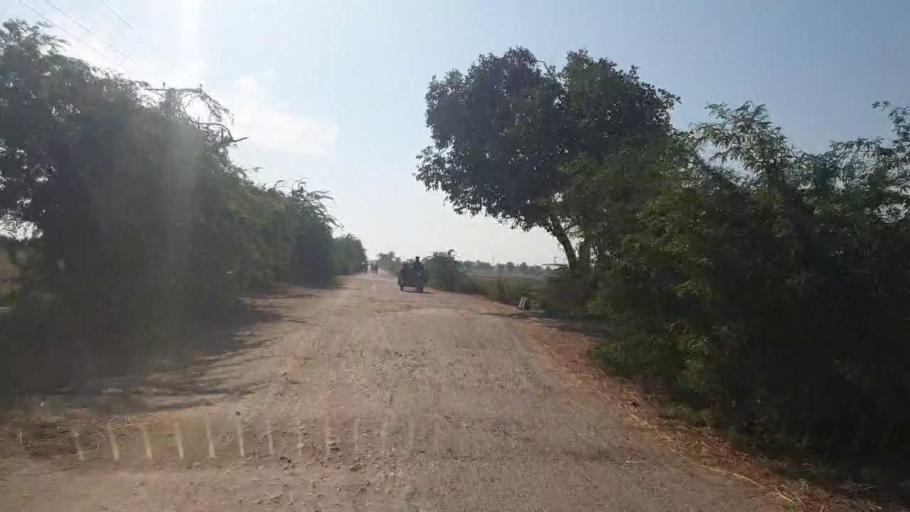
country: PK
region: Sindh
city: Talhar
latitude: 24.9038
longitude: 68.8225
